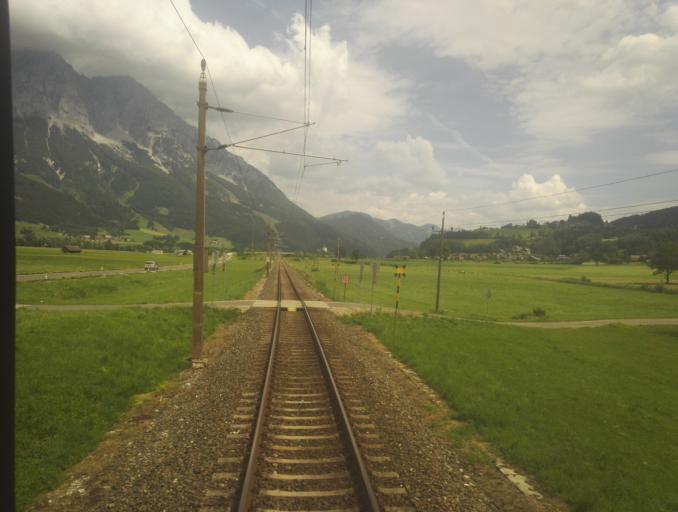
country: AT
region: Styria
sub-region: Politischer Bezirk Liezen
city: Niederoblarn
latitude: 47.4710
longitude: 14.0089
